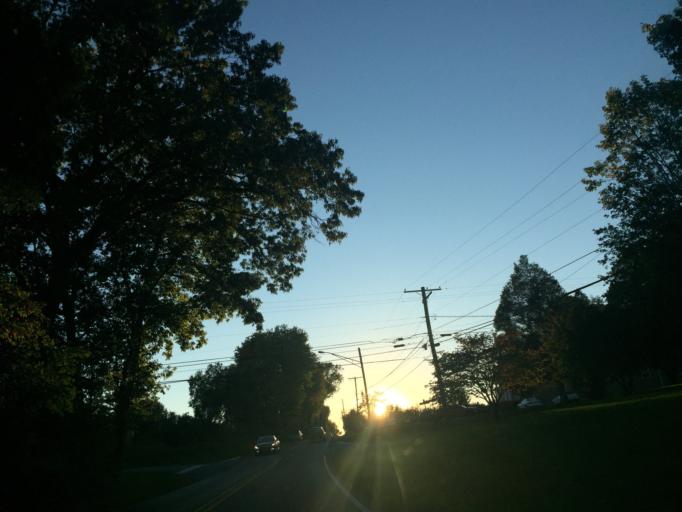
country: US
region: Maryland
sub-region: Harford County
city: Joppatowne
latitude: 39.4702
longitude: -76.3461
